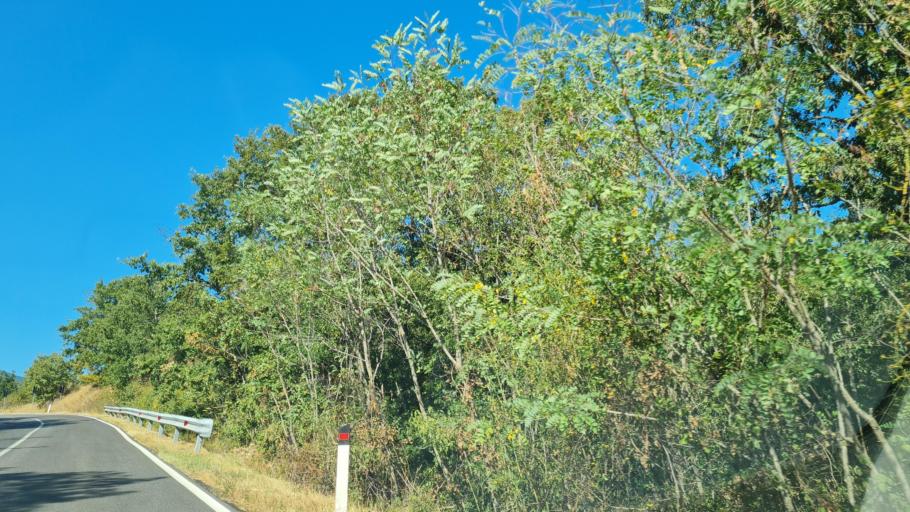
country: IT
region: Tuscany
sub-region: Provincia di Siena
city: Abbadia San Salvatore
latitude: 42.9150
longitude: 11.6902
